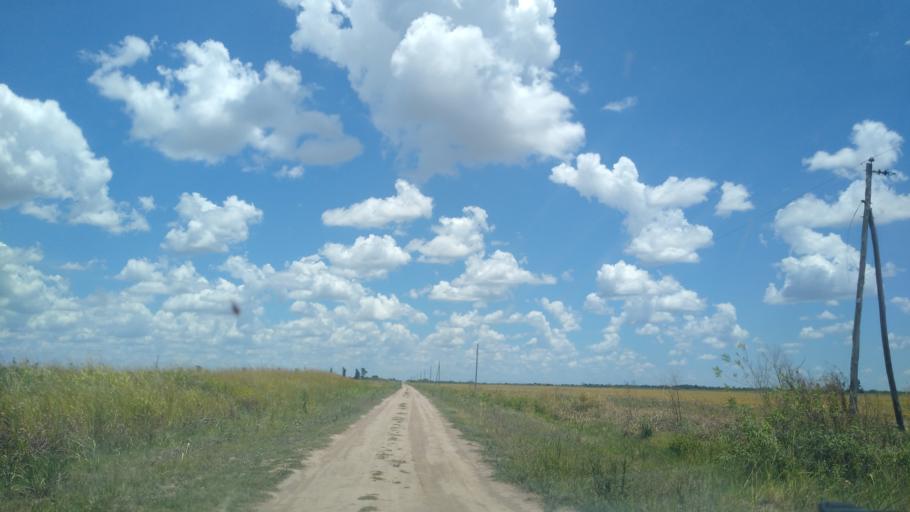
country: AR
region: Chaco
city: Presidencia Roque Saenz Pena
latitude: -26.7448
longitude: -60.3465
